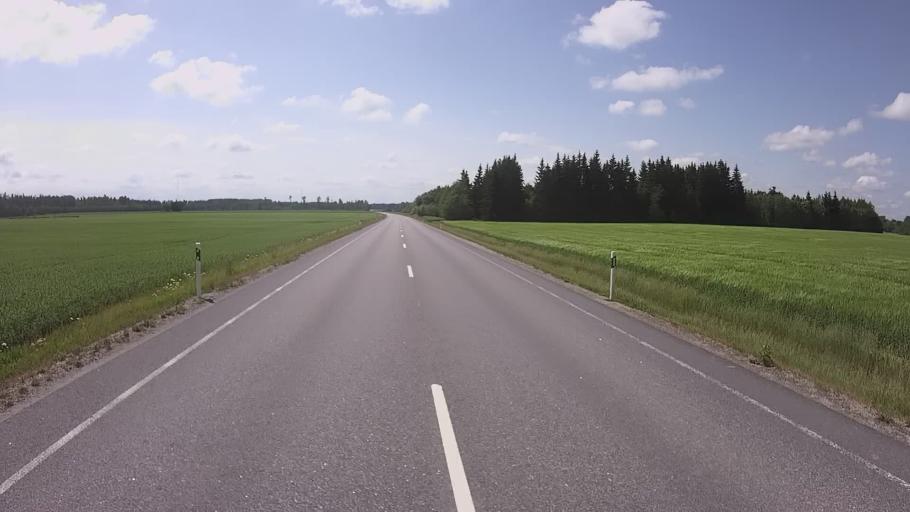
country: EE
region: Tartu
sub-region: Tartu linn
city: Tartu
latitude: 58.3928
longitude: 26.8927
